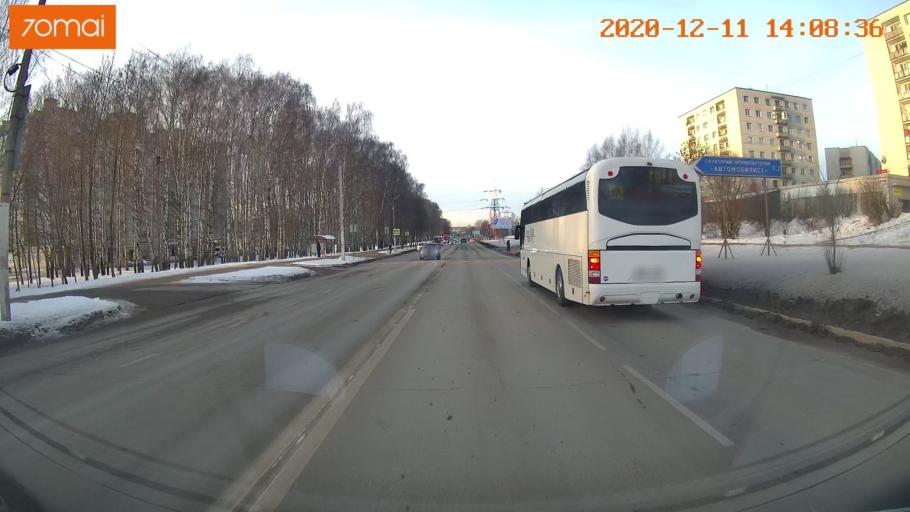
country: RU
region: Kostroma
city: Oktyabr'skiy
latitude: 57.7367
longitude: 40.9940
